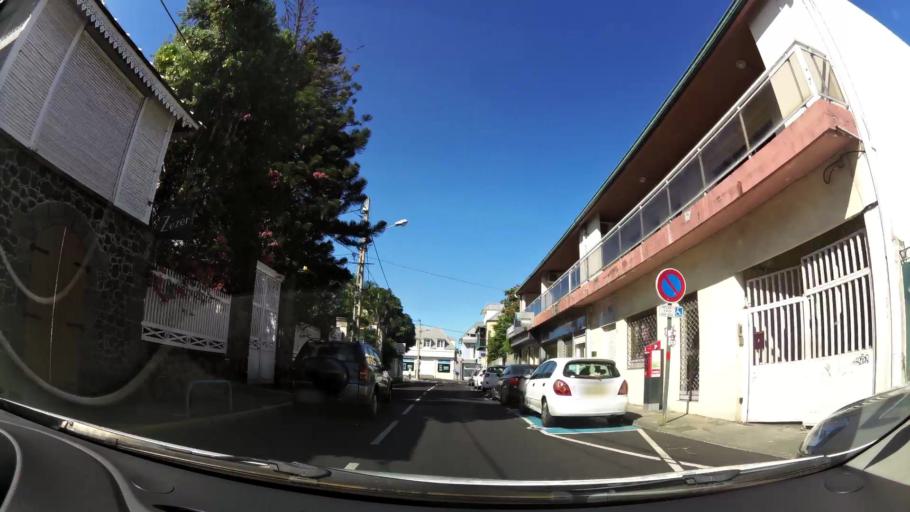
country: RE
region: Reunion
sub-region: Reunion
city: Saint-Pierre
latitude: -21.3388
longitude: 55.4787
